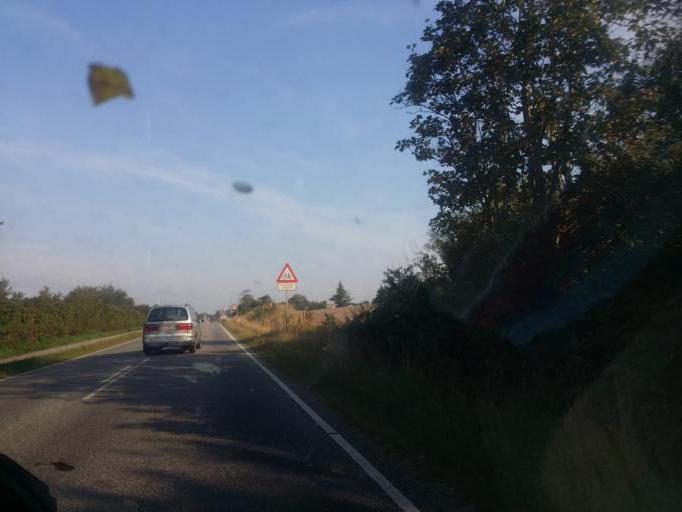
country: DK
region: South Denmark
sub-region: Tonder Kommune
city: Sherrebek
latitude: 55.1468
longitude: 8.7843
